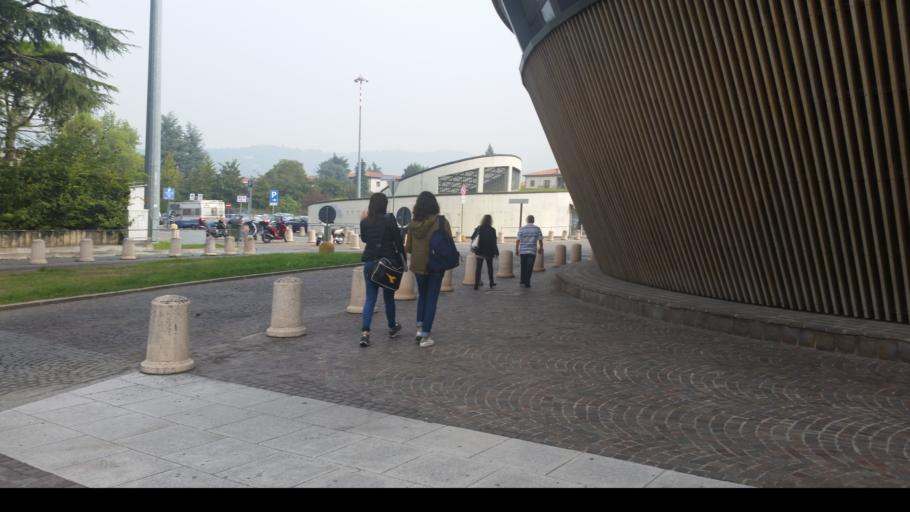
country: IT
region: Lombardy
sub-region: Provincia di Brescia
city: Brescia
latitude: 45.5599
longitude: 10.2317
